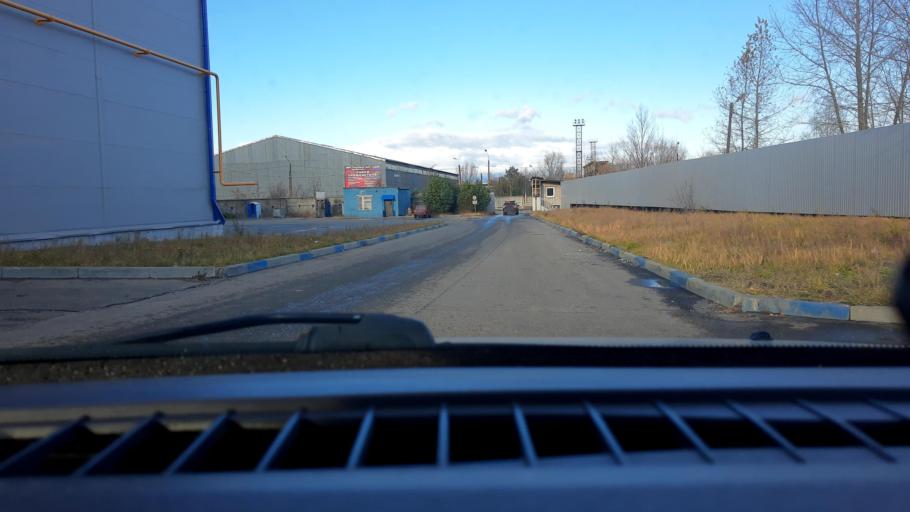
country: RU
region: Nizjnij Novgorod
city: Gorbatovka
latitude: 56.3486
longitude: 43.8094
